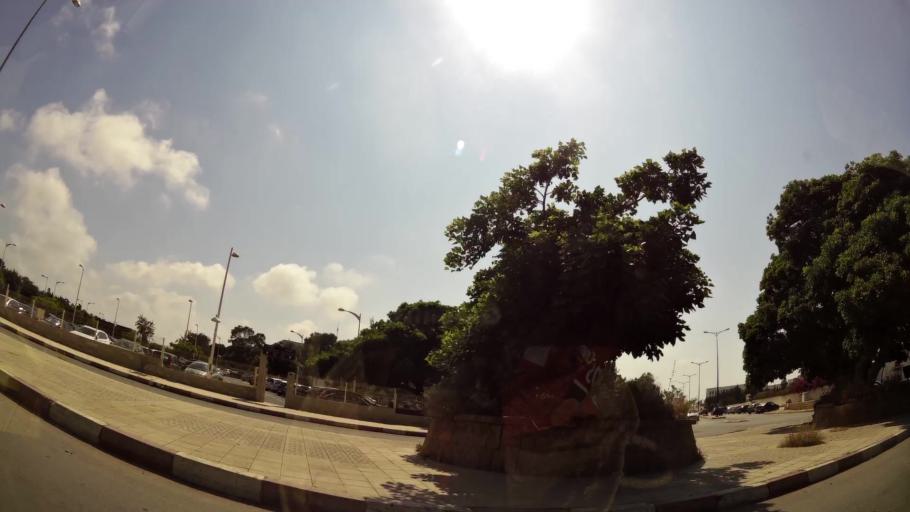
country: MA
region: Rabat-Sale-Zemmour-Zaer
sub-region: Rabat
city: Rabat
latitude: 33.9813
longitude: -6.8650
